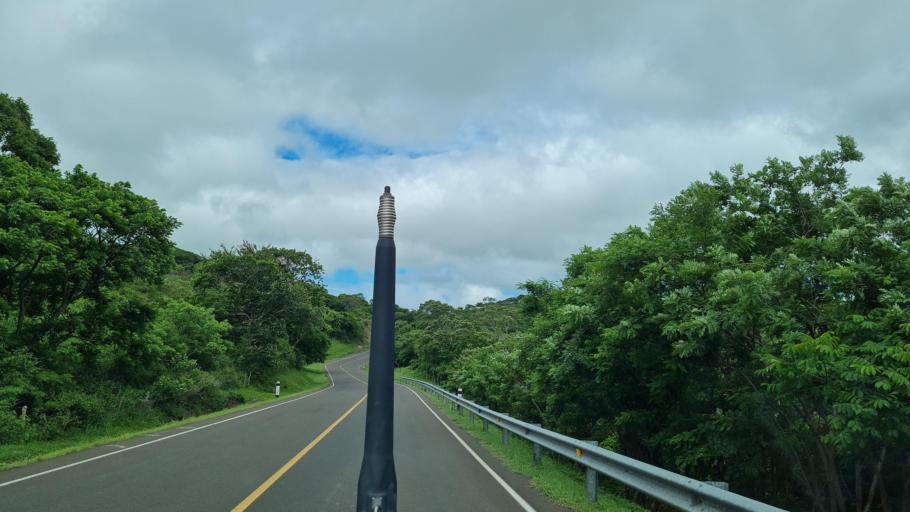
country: NI
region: Matagalpa
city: Terrabona
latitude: 12.5932
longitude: -85.9510
